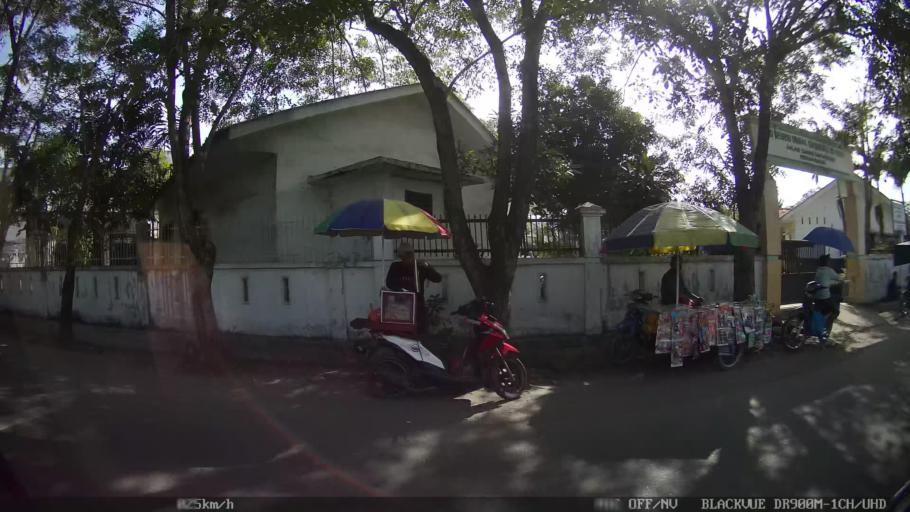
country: ID
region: North Sumatra
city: Medan
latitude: 3.6033
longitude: 98.6596
